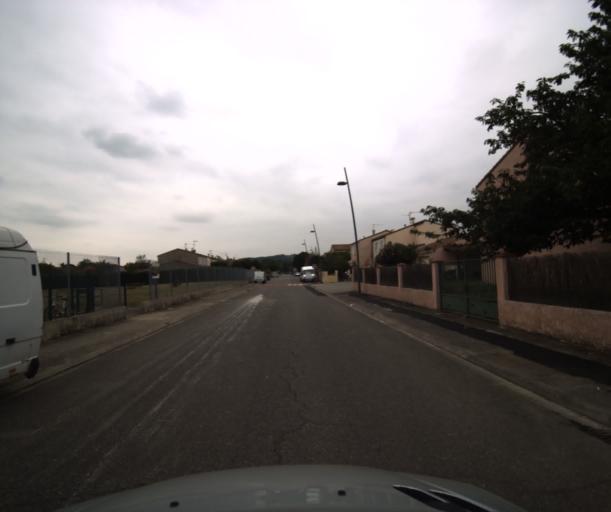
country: FR
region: Midi-Pyrenees
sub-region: Departement de la Haute-Garonne
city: Portet-sur-Garonne
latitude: 43.5428
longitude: 1.4108
